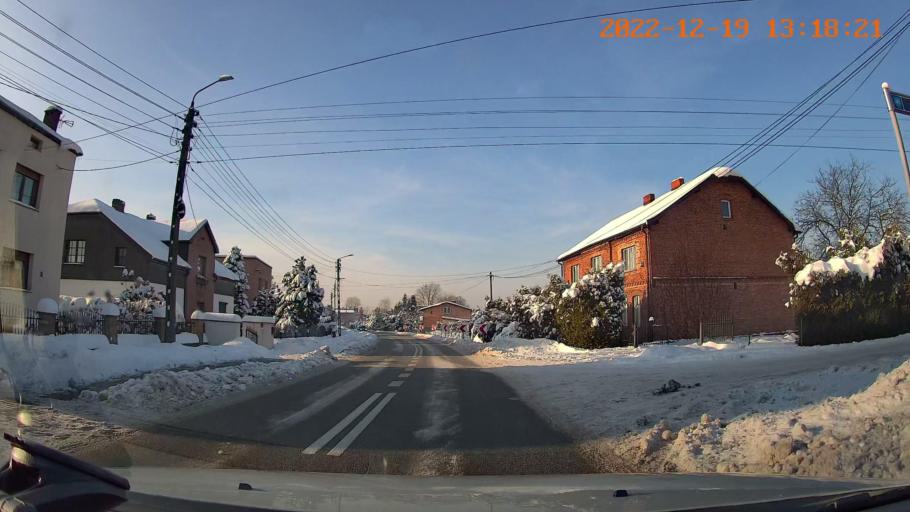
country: PL
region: Silesian Voivodeship
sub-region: Powiat bierunsko-ledzinski
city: Chelm Slaski
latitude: 50.1061
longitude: 19.1993
